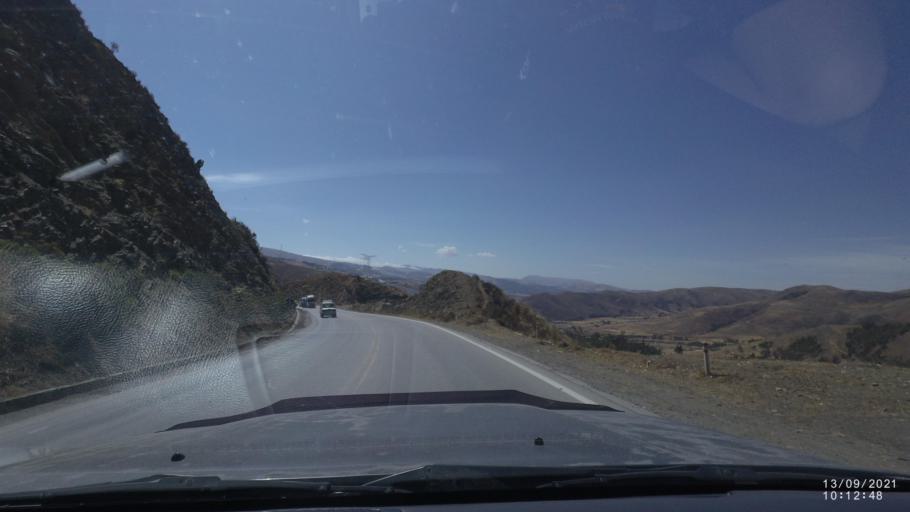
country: BO
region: Cochabamba
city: Colomi
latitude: -17.3917
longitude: -65.8345
